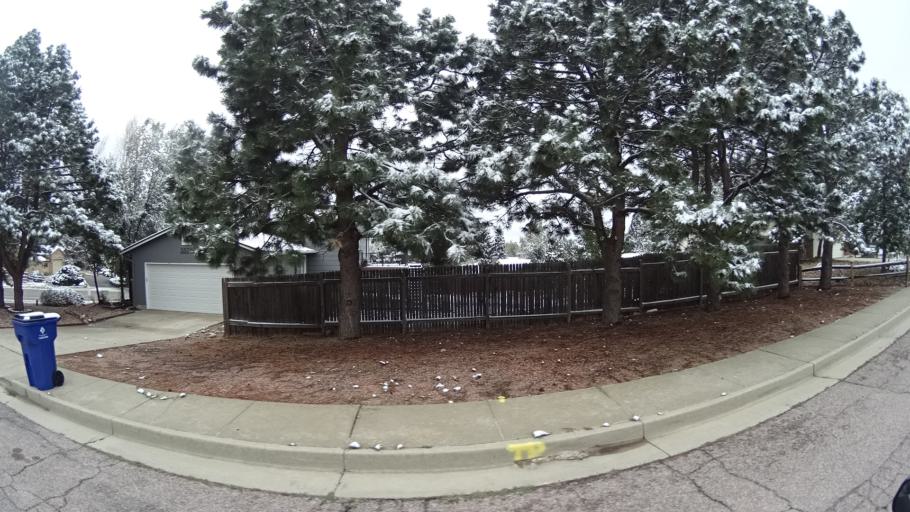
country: US
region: Colorado
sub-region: El Paso County
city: Cimarron Hills
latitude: 38.9118
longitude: -104.7610
